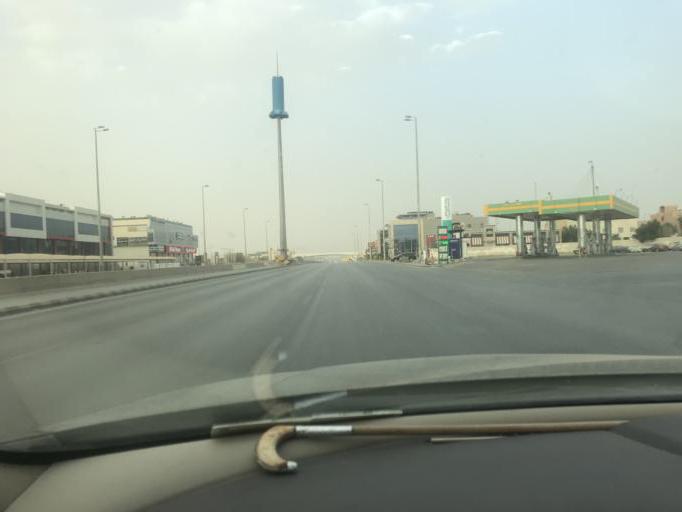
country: SA
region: Ar Riyad
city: Riyadh
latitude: 24.8077
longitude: 46.6639
